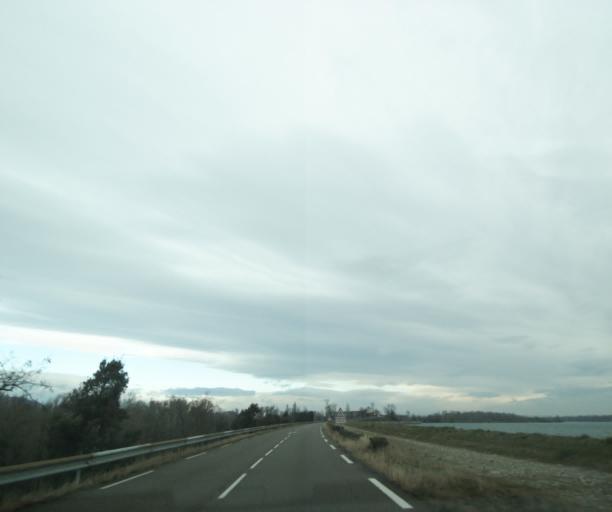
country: FR
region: Rhone-Alpes
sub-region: Departement de l'Ardeche
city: Cornas
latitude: 44.9806
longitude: 4.8562
